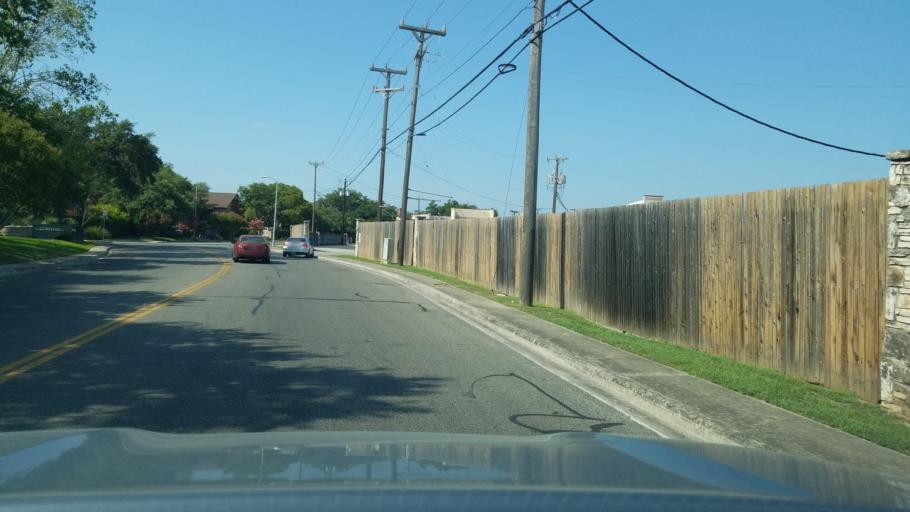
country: US
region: Texas
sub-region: Bexar County
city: Hollywood Park
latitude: 29.5621
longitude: -98.4810
